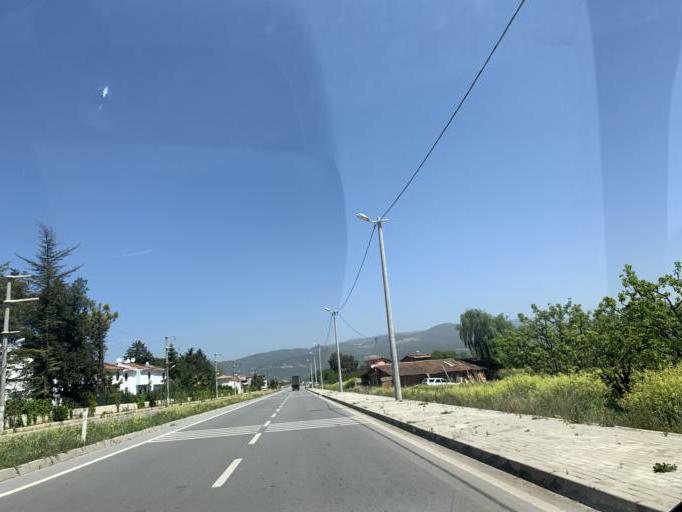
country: TR
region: Bursa
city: Iznik
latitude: 40.4080
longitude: 29.7050
